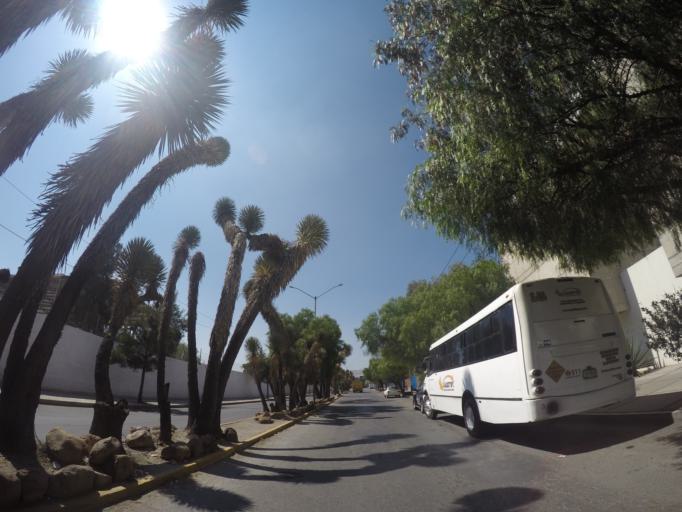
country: MX
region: San Luis Potosi
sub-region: San Luis Potosi
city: San Luis Potosi
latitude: 22.1438
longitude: -101.0139
